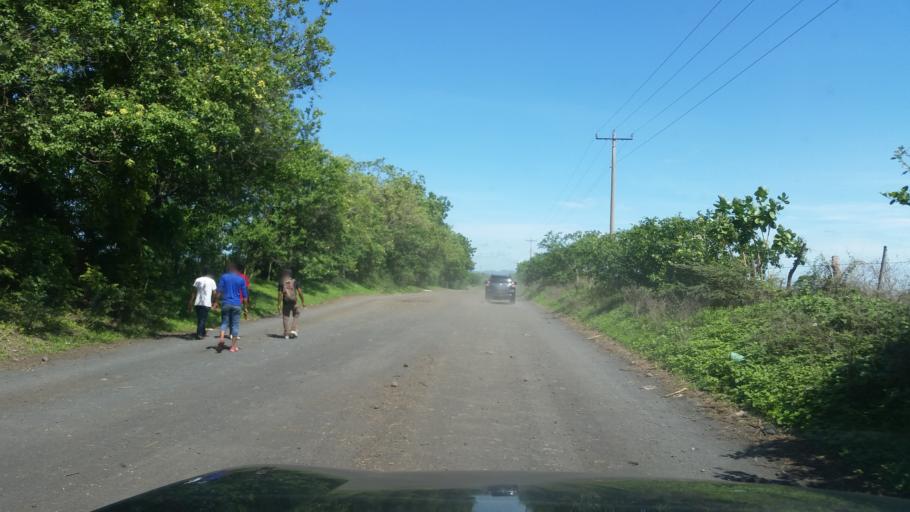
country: NI
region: Chinandega
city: Puerto Morazan
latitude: 12.7680
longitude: -87.0637
